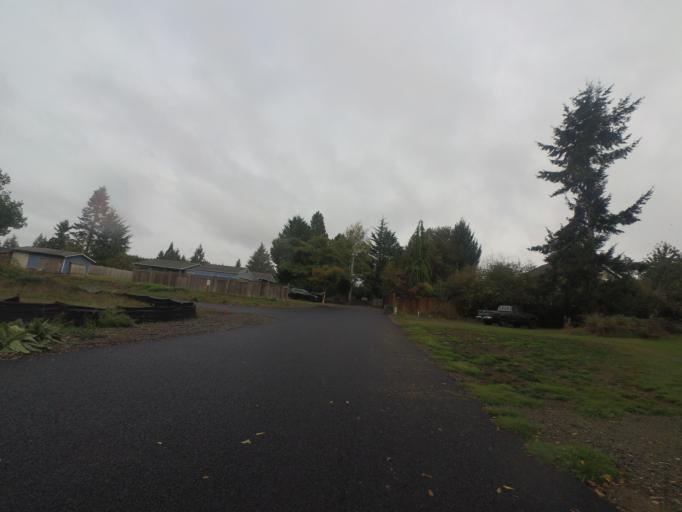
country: US
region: Washington
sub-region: Pierce County
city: University Place
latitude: 47.2249
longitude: -122.5422
